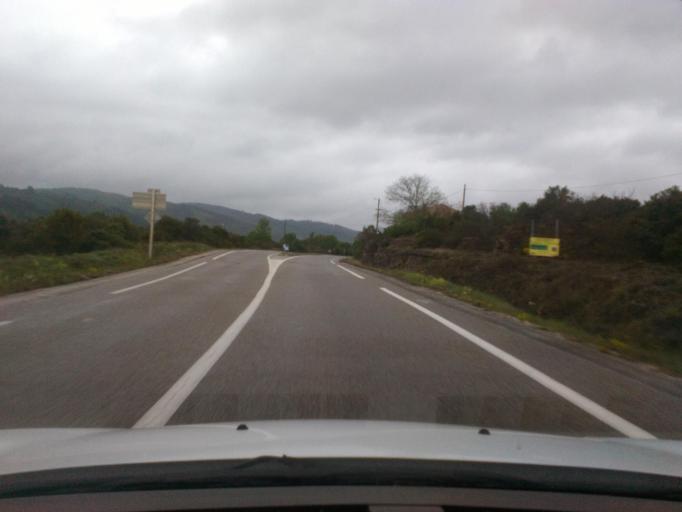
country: FR
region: Languedoc-Roussillon
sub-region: Departement du Gard
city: Saint-Ambroix
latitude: 44.2944
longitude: 4.1805
